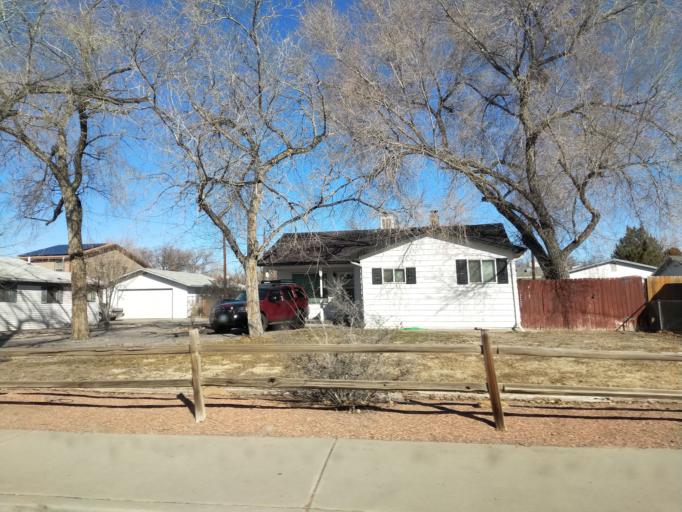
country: US
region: Colorado
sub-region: Mesa County
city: Grand Junction
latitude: 39.0702
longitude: -108.5446
